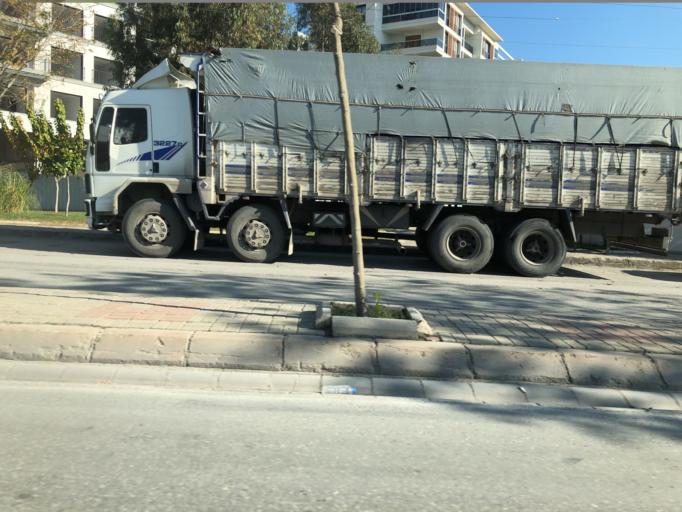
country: TR
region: Izmir
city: Izmir
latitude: 38.4587
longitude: 27.1748
